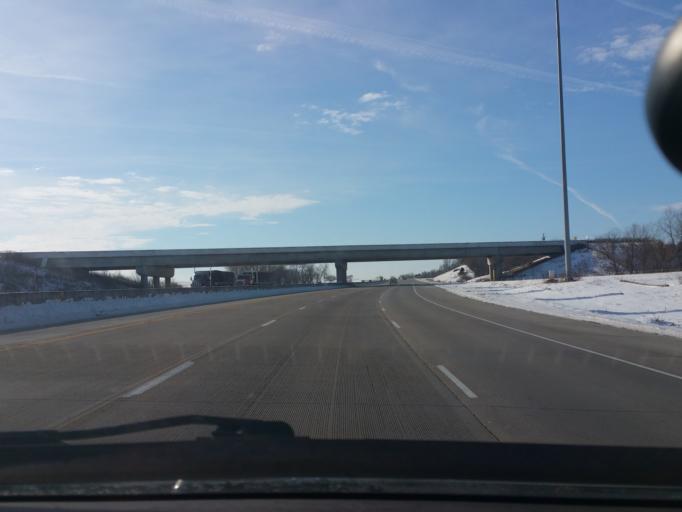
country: US
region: Iowa
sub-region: Polk County
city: West Des Moines
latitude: 41.5210
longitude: -93.7738
